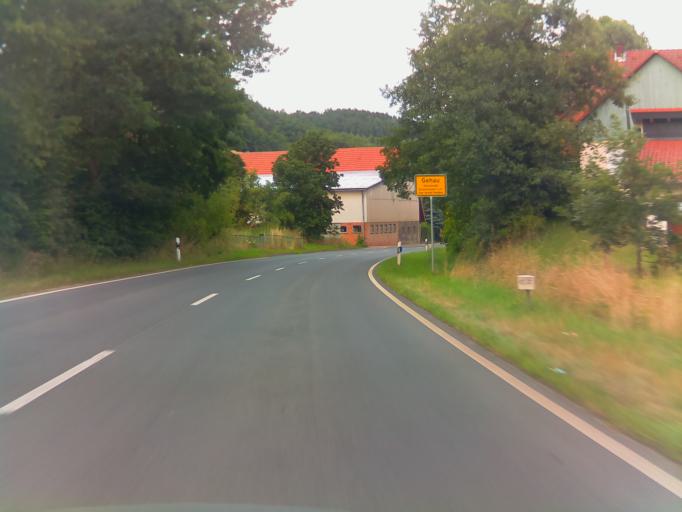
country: DE
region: Hesse
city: Grebenau
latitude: 50.7792
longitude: 9.4721
